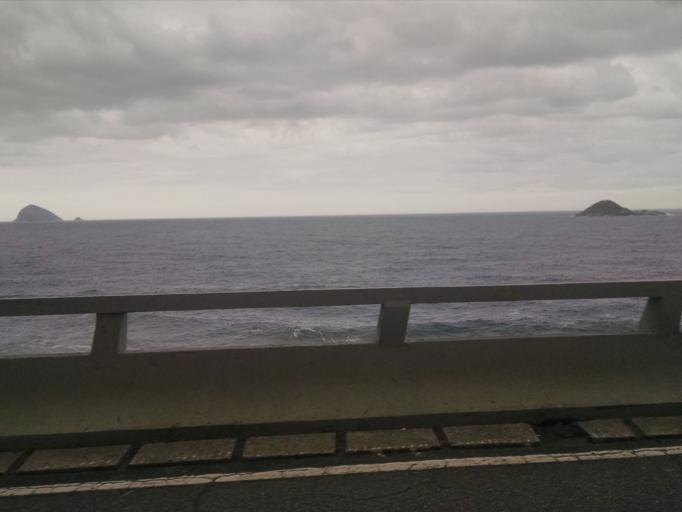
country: BR
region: Rio de Janeiro
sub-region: Rio De Janeiro
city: Rio de Janeiro
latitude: -23.0052
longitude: -43.2792
